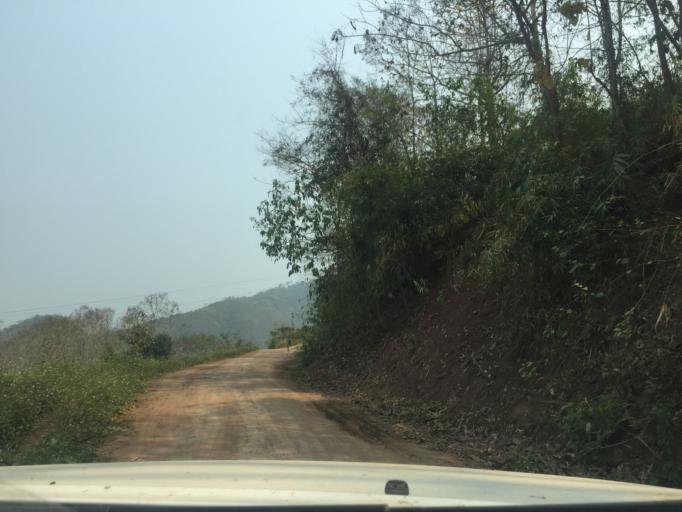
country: LA
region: Loungnamtha
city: Muang Nale
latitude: 20.3006
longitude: 101.6592
